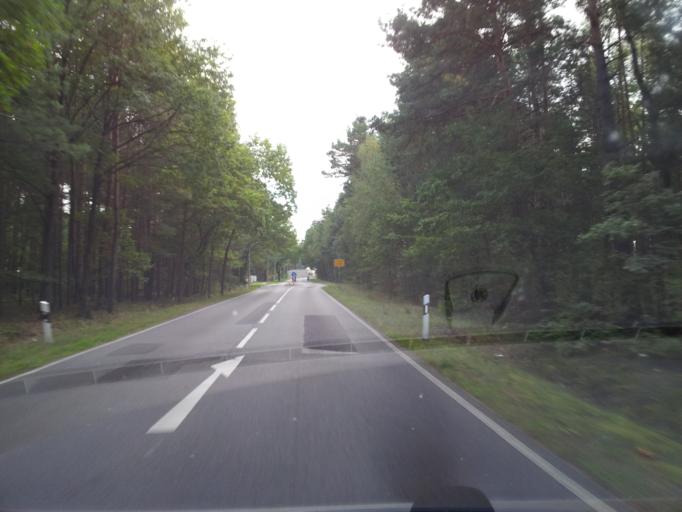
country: DE
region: Brandenburg
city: Sallgast
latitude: 51.6029
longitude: 13.7757
